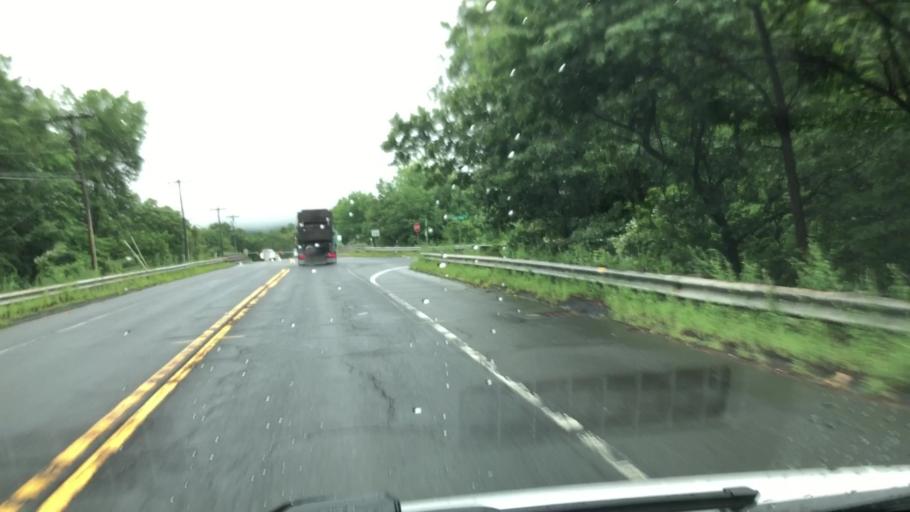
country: US
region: Massachusetts
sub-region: Franklin County
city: South Deerfield
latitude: 42.4685
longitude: -72.6107
